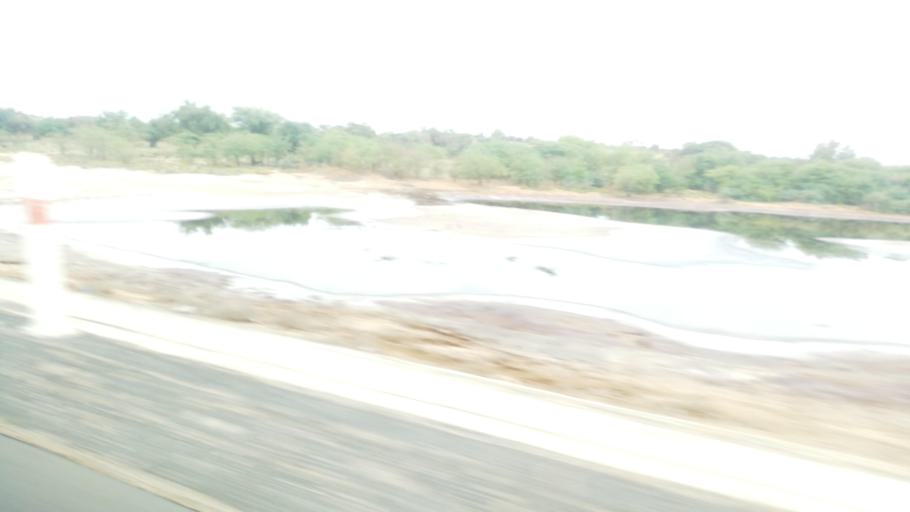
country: SN
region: Saint-Louis
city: Saint-Louis
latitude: 16.0745
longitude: -16.3850
